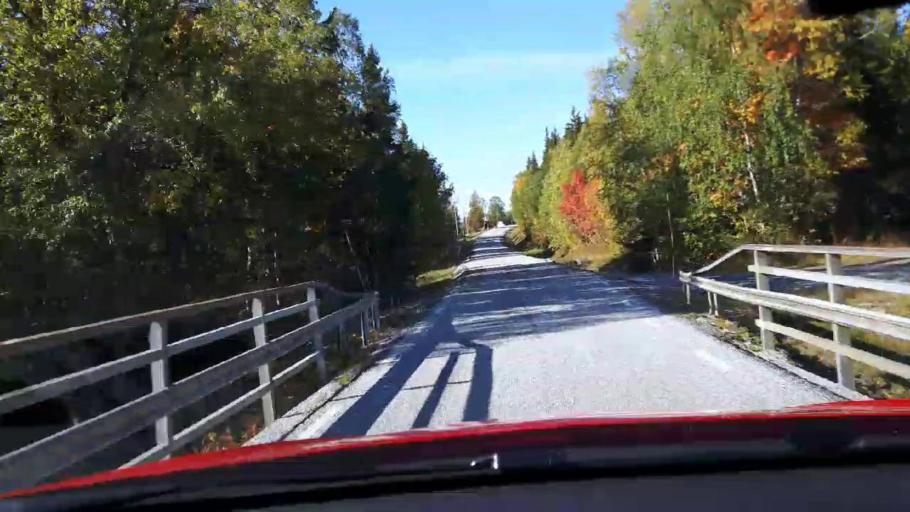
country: NO
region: Nord-Trondelag
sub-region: Royrvik
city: Royrvik
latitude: 64.8279
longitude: 14.1238
